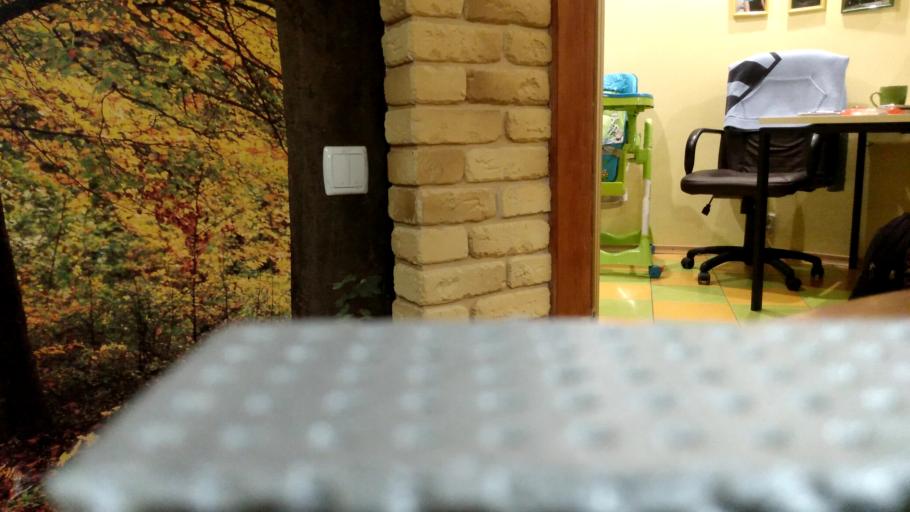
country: RU
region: Republic of Karelia
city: Pudozh
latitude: 61.9432
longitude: 37.6200
